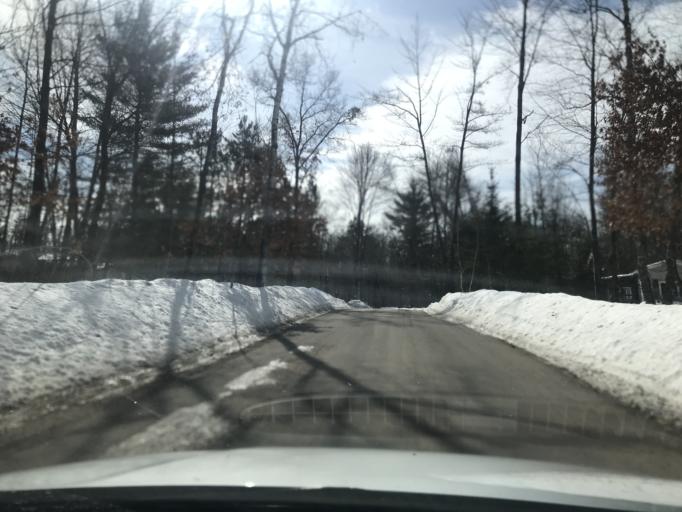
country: US
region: Wisconsin
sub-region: Menominee County
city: Legend Lake
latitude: 45.1147
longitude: -88.4439
